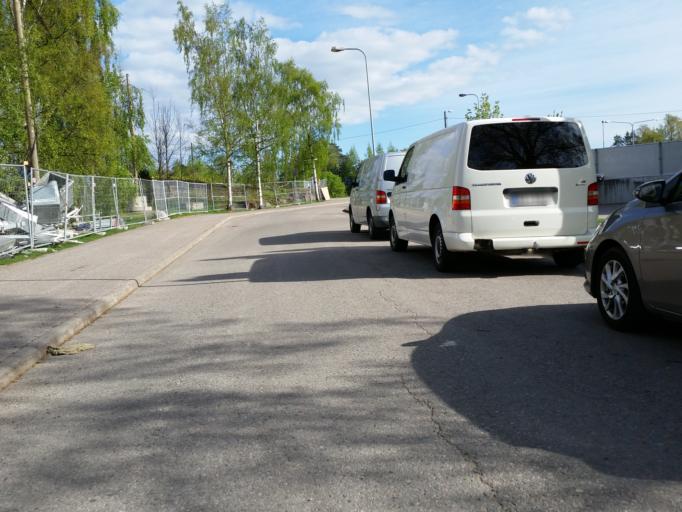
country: FI
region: Uusimaa
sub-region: Helsinki
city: Koukkuniemi
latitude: 60.1692
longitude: 24.7757
